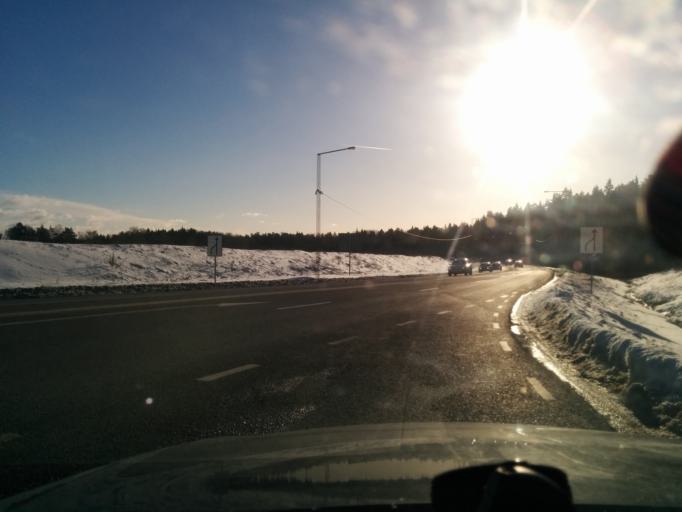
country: SE
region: Stockholm
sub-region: Taby Kommun
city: Taby
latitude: 59.4723
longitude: 18.1170
